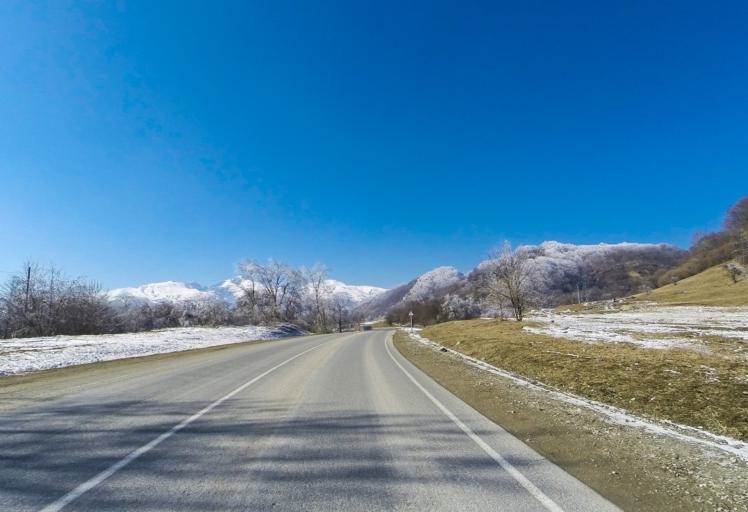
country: RU
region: Kabardino-Balkariya
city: Babugent
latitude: 43.2917
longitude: 43.5694
